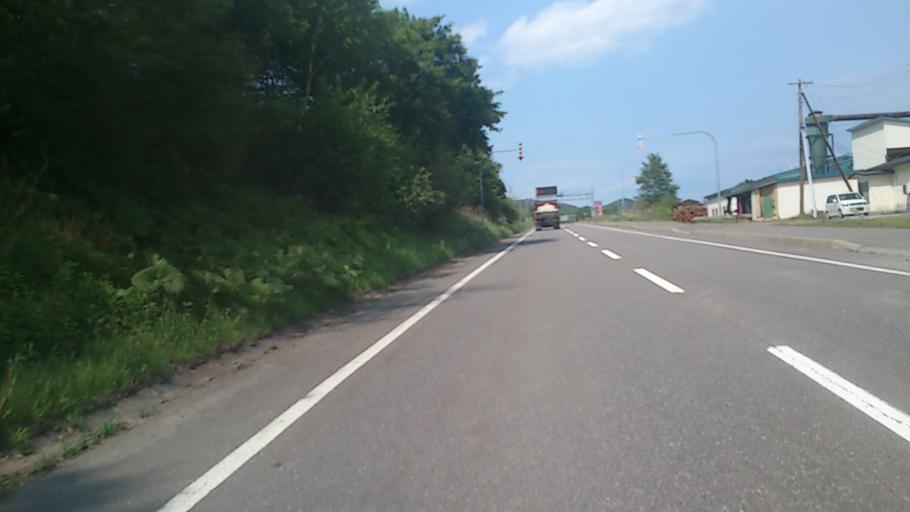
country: JP
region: Hokkaido
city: Otofuke
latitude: 43.2482
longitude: 143.5622
